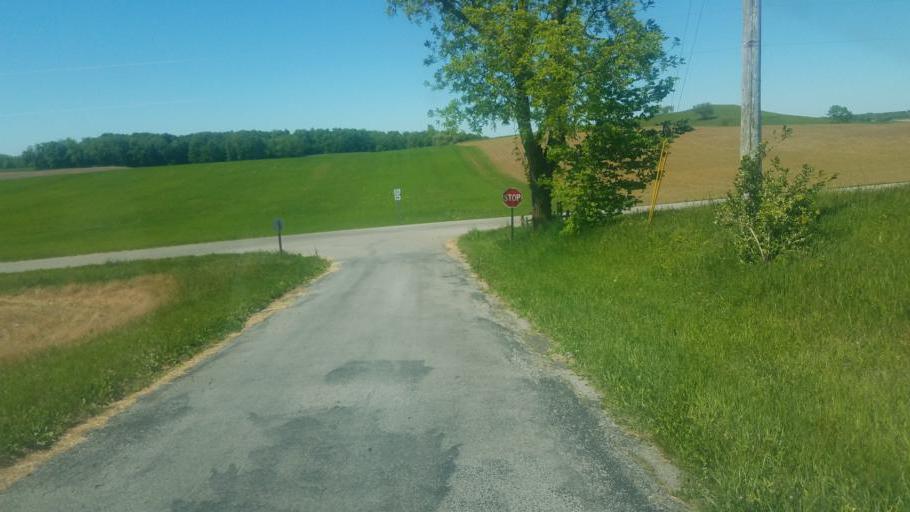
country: US
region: Ohio
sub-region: Logan County
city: De Graff
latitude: 40.2939
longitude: -83.8523
